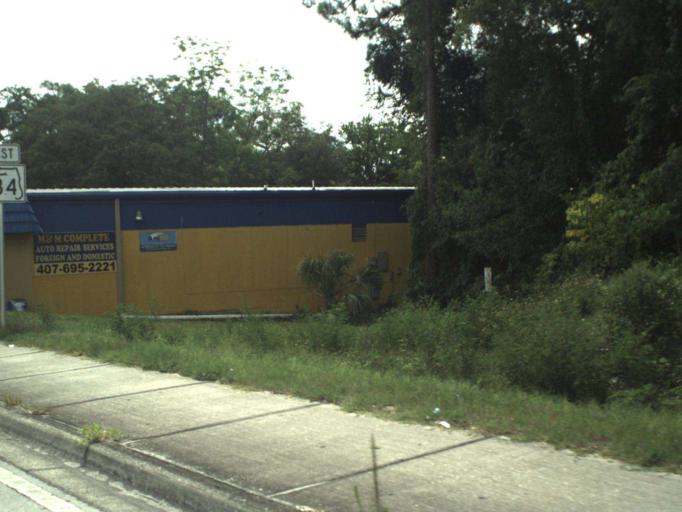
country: US
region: Florida
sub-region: Seminole County
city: Longwood
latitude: 28.6978
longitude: -81.3255
